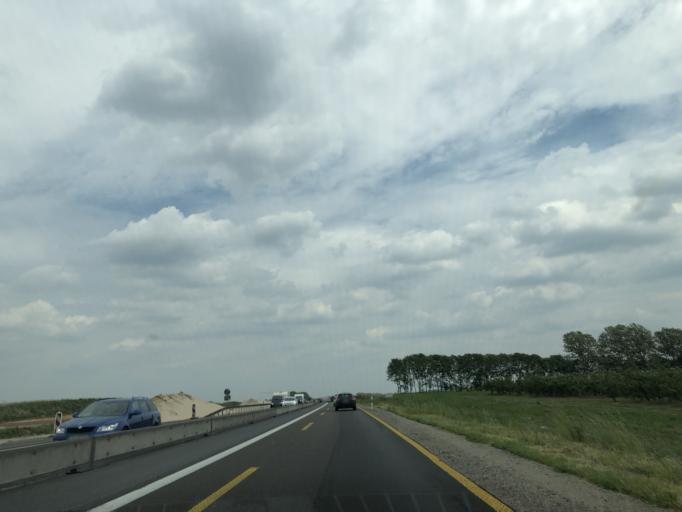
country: DE
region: Brandenburg
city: Kremmen
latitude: 52.7040
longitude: 13.0730
